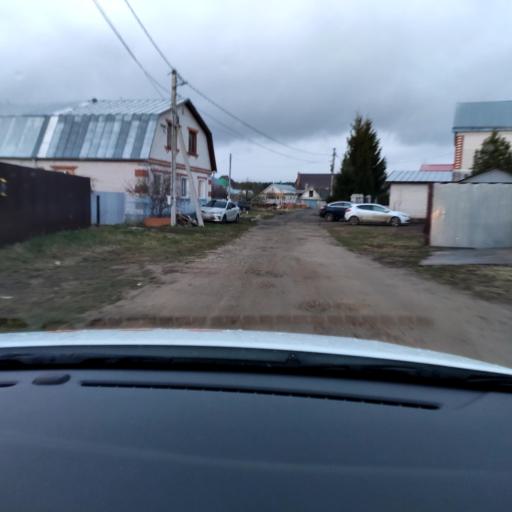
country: RU
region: Tatarstan
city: Stolbishchi
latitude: 55.6945
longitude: 49.1563
